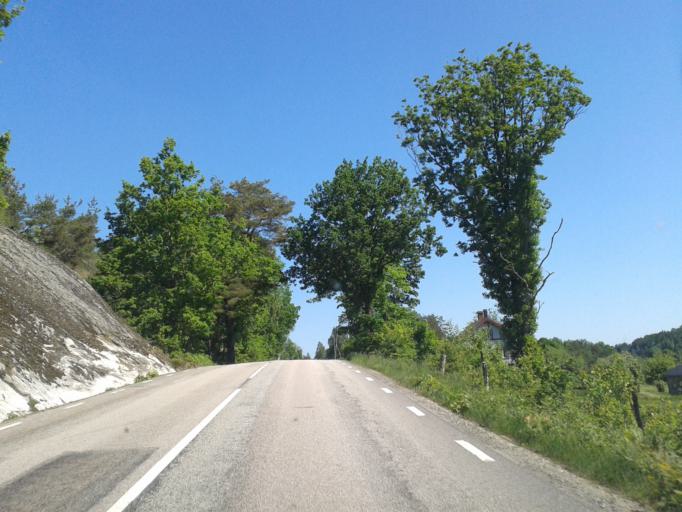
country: SE
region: Vaestra Goetaland
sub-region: Orust
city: Henan
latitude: 58.2412
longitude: 11.7140
